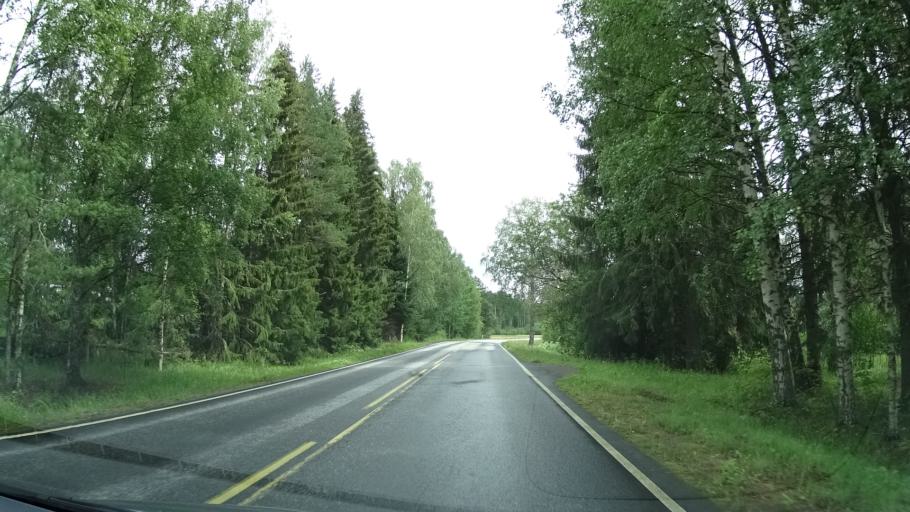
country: FI
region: Pirkanmaa
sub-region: Etelae-Pirkanmaa
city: Urjala
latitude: 61.0933
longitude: 23.3792
